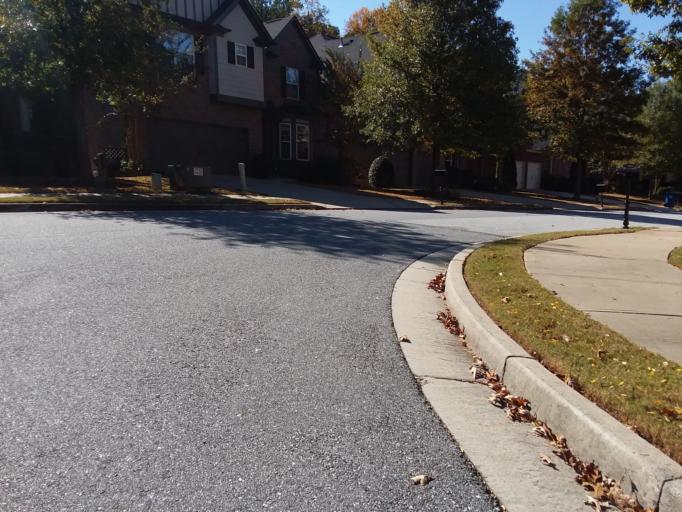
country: US
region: Georgia
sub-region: Fulton County
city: Johns Creek
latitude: 34.0250
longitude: -84.2471
